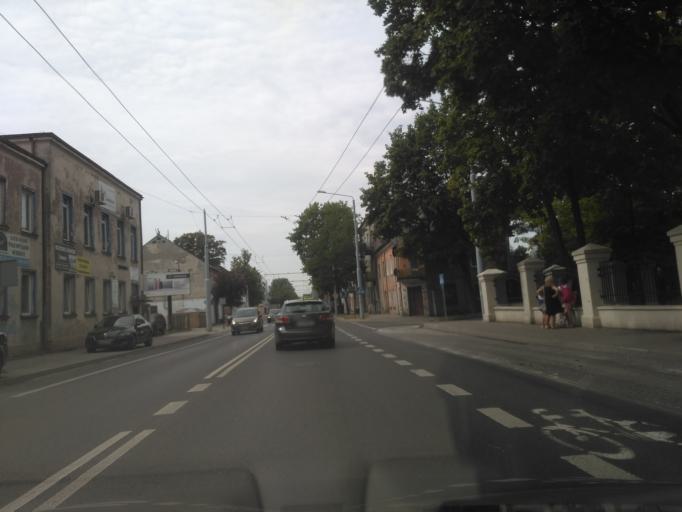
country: PL
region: Lublin Voivodeship
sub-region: Powiat lubelski
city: Lublin
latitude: 51.2264
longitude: 22.5532
